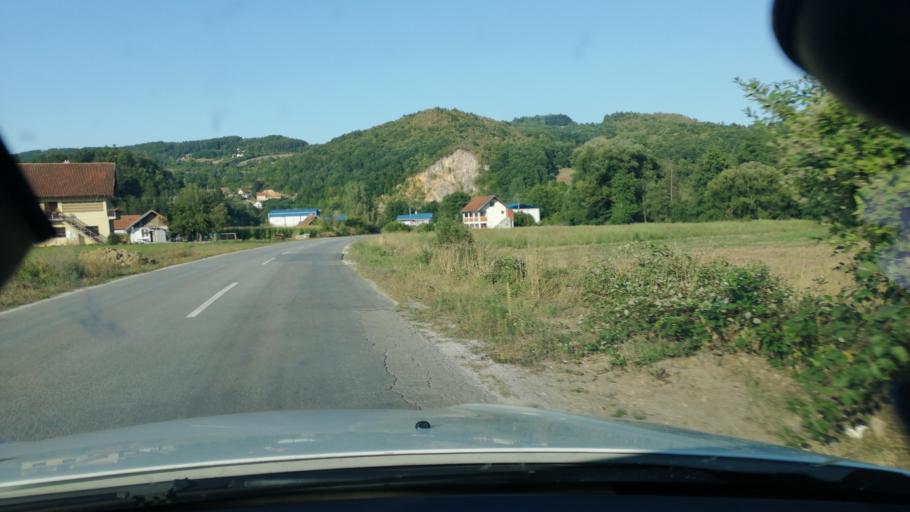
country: RS
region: Central Serbia
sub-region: Moravicki Okrug
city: Ivanjica
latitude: 43.7092
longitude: 20.2391
